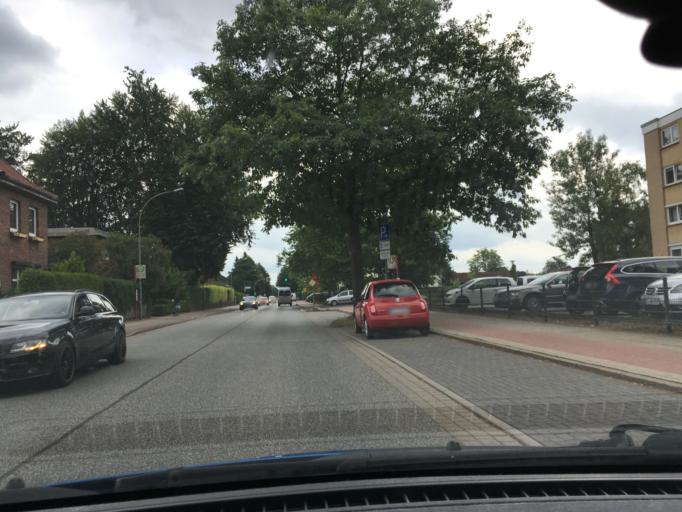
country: DE
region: Lower Saxony
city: Tostedt
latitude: 53.2771
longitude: 9.7170
